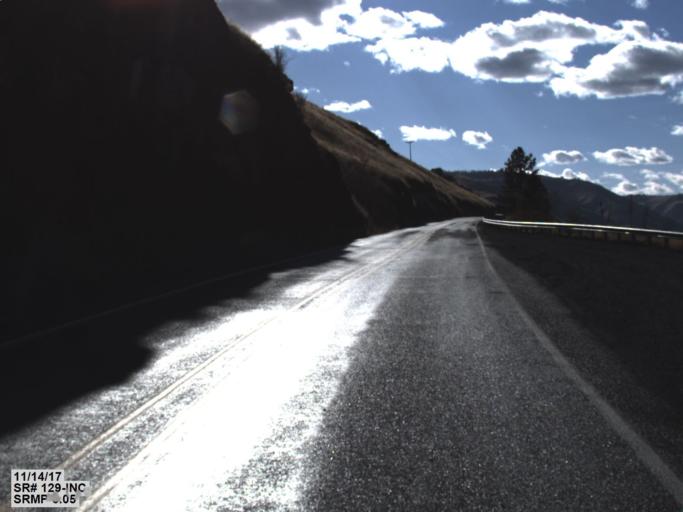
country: US
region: Washington
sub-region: Asotin County
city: Asotin
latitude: 46.0535
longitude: -117.2377
